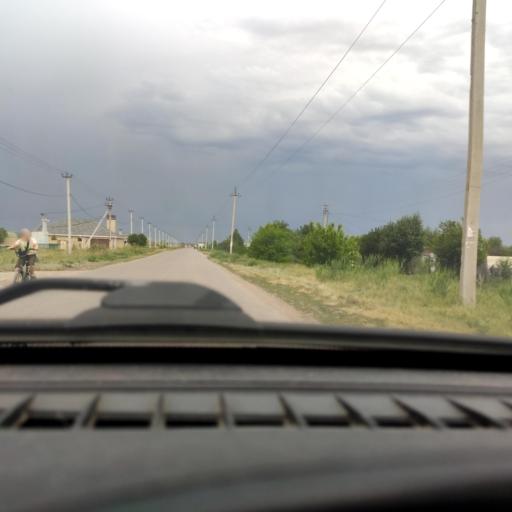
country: RU
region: Samara
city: Tol'yatti
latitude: 53.6437
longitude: 49.3269
